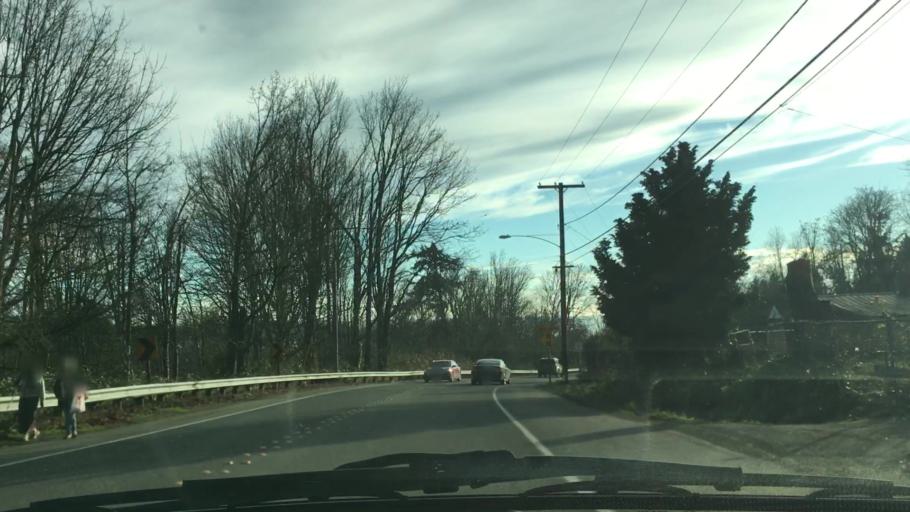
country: US
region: Washington
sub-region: King County
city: Des Moines
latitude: 47.4109
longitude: -122.3264
